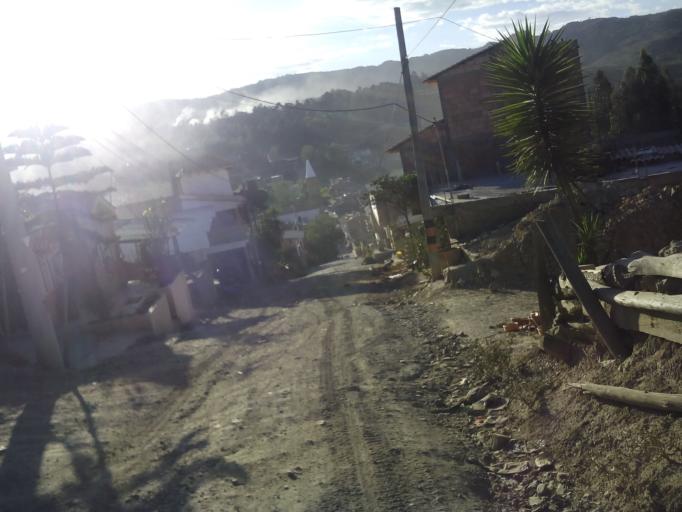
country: CO
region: Boyaca
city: Raquira
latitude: 5.5379
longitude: -73.6305
